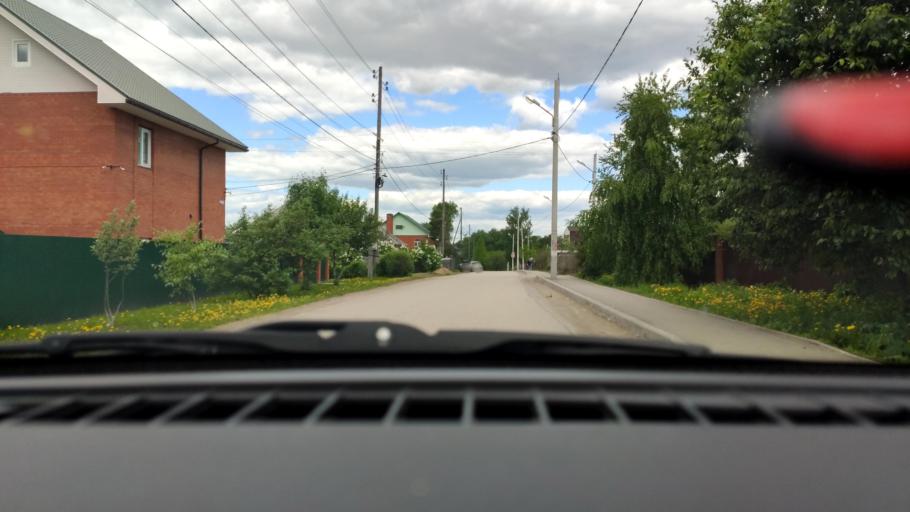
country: RU
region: Perm
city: Perm
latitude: 58.0452
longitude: 56.3592
